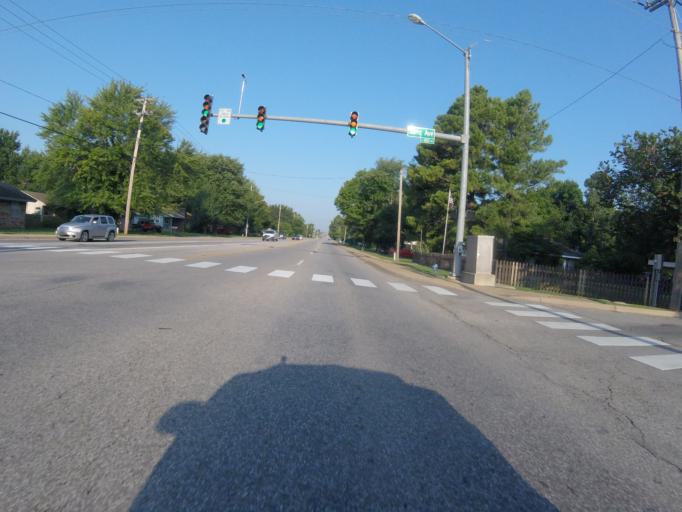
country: US
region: Arkansas
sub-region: Washington County
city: Fayetteville
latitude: 36.0780
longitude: -94.1887
